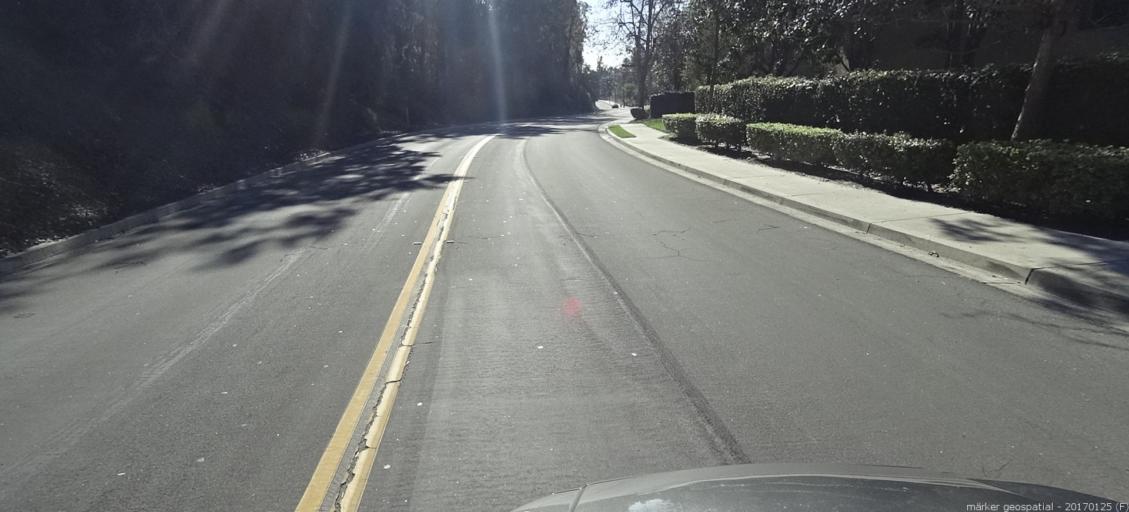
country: US
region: California
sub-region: Orange County
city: Lake Forest
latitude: 33.6592
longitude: -117.6737
